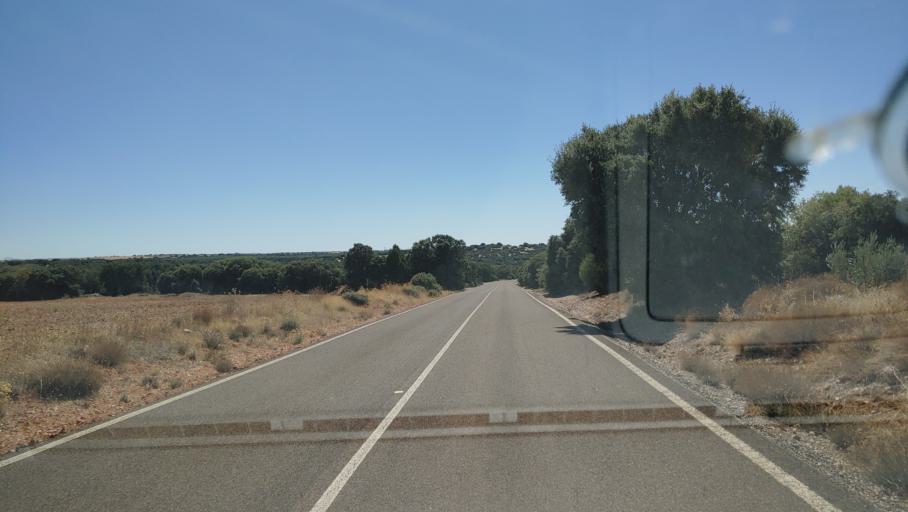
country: ES
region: Castille-La Mancha
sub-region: Provincia de Ciudad Real
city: Villahermosa
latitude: 38.8108
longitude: -2.8356
